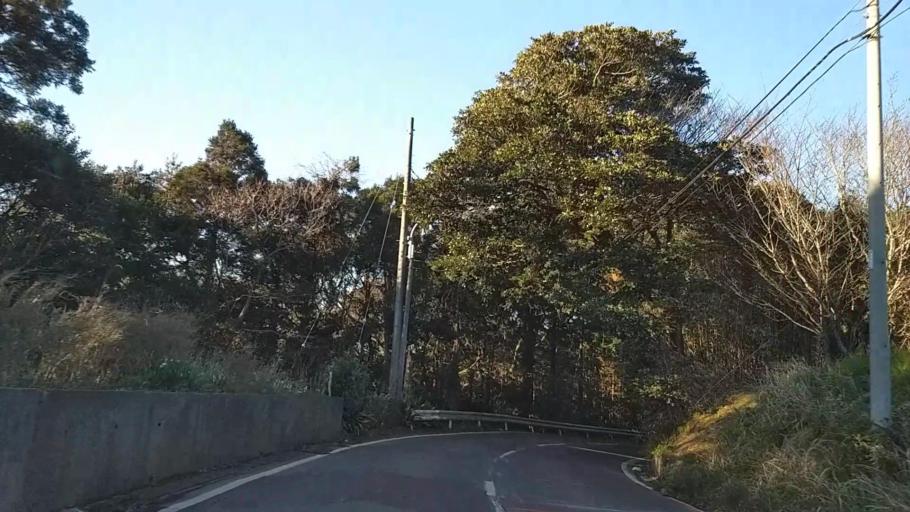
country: JP
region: Chiba
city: Asahi
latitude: 35.7434
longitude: 140.7337
